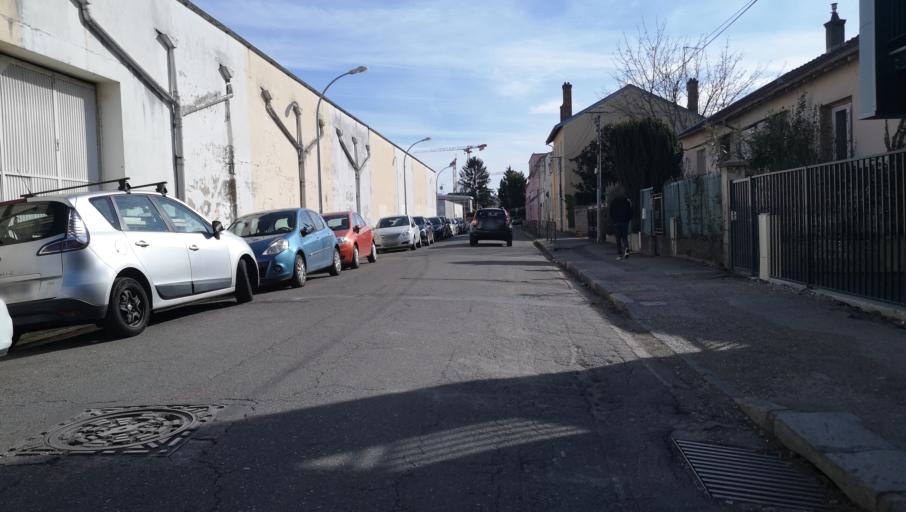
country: FR
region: Rhone-Alpes
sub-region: Departement du Rhone
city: Villeurbanne
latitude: 45.7763
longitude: 4.8765
